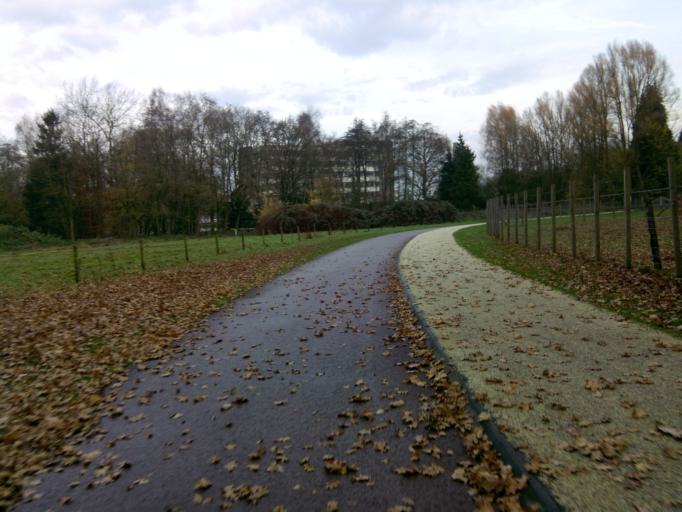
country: NL
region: Utrecht
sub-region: Gemeente Amersfoort
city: Randenbroek
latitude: 52.1435
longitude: 5.4019
